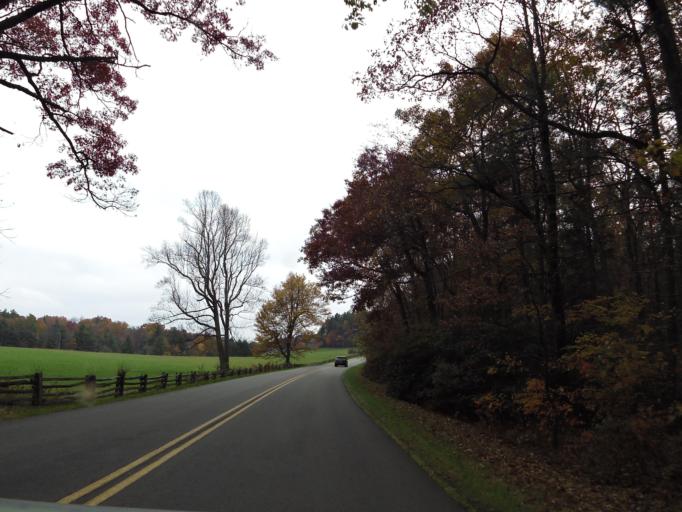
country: US
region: North Carolina
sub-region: Ashe County
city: Jefferson
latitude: 36.3551
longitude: -81.3725
